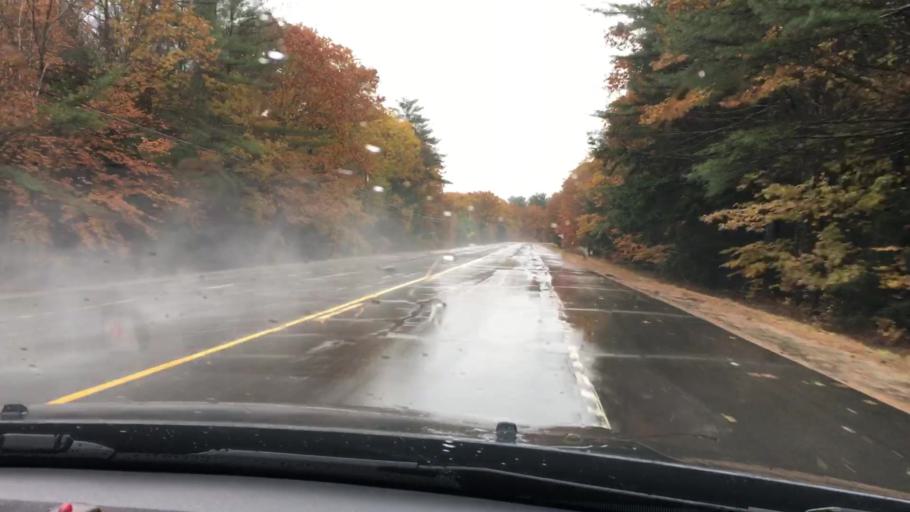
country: US
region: New Hampshire
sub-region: Grafton County
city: Ashland
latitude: 43.7160
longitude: -71.6248
